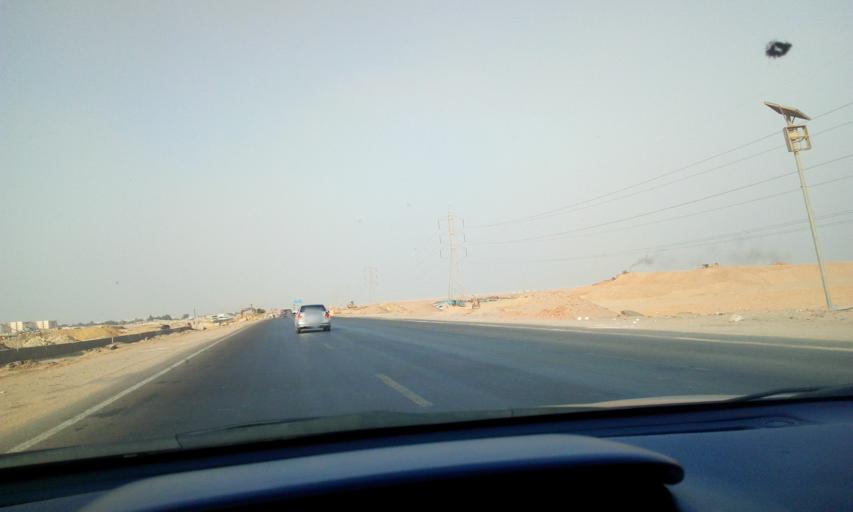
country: EG
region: Al Jizah
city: Madinat Sittah Uktubar
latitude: 29.8648
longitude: 31.0706
